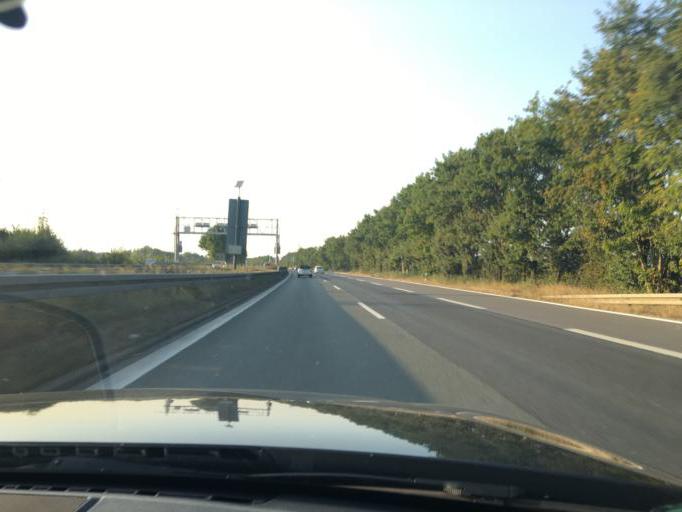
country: DE
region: Bavaria
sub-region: Upper Franconia
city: Eggolsheim
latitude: 49.7574
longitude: 11.0584
